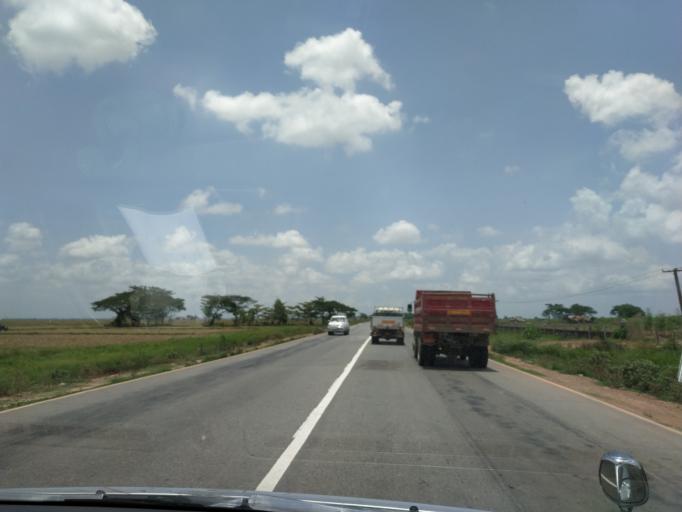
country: MM
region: Bago
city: Bago
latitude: 17.4650
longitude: 96.5881
